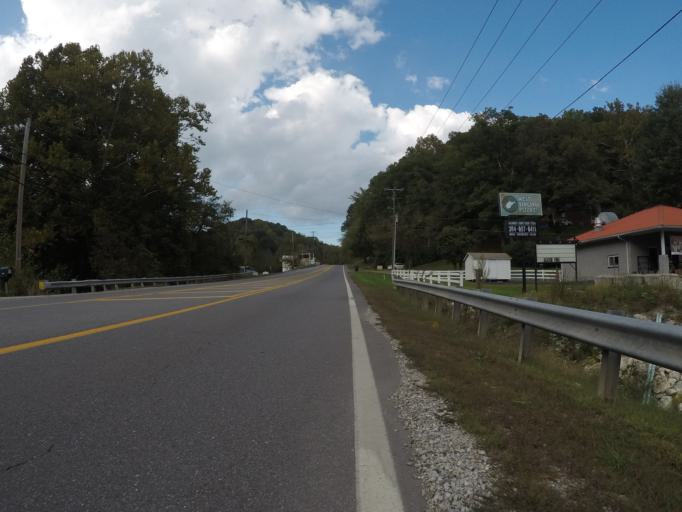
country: US
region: West Virginia
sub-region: Wayne County
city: Lavalette
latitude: 38.3483
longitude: -82.4522
